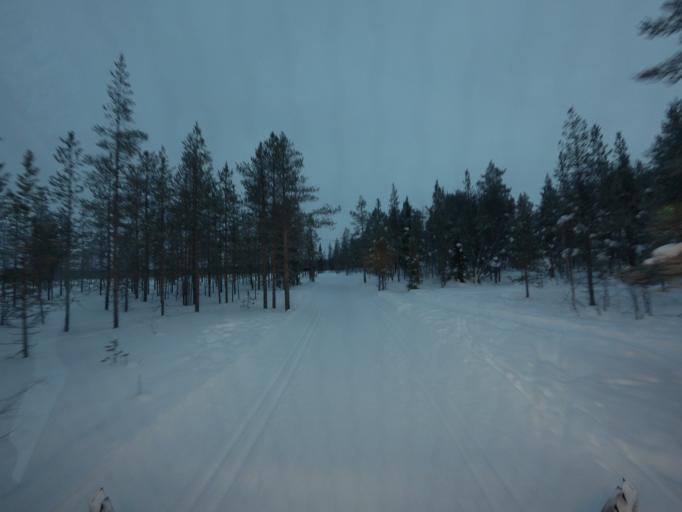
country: FI
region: Lapland
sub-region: Tunturi-Lappi
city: Kolari
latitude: 67.6095
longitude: 24.1733
